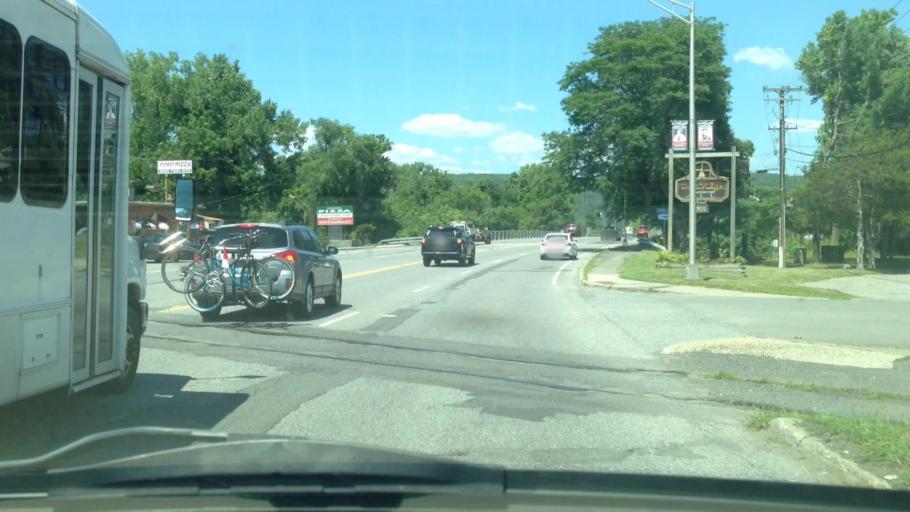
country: US
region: New York
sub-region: Ulster County
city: Kingston
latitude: 41.9382
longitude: -74.0266
